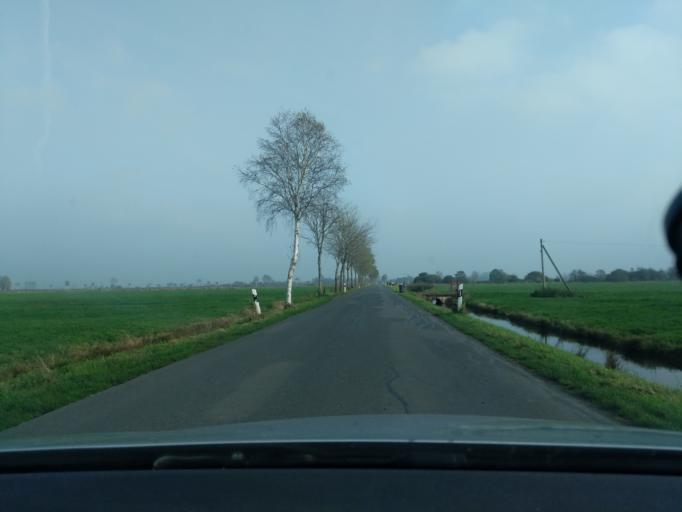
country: DE
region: Lower Saxony
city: Wanna
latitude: 53.7254
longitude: 8.8019
